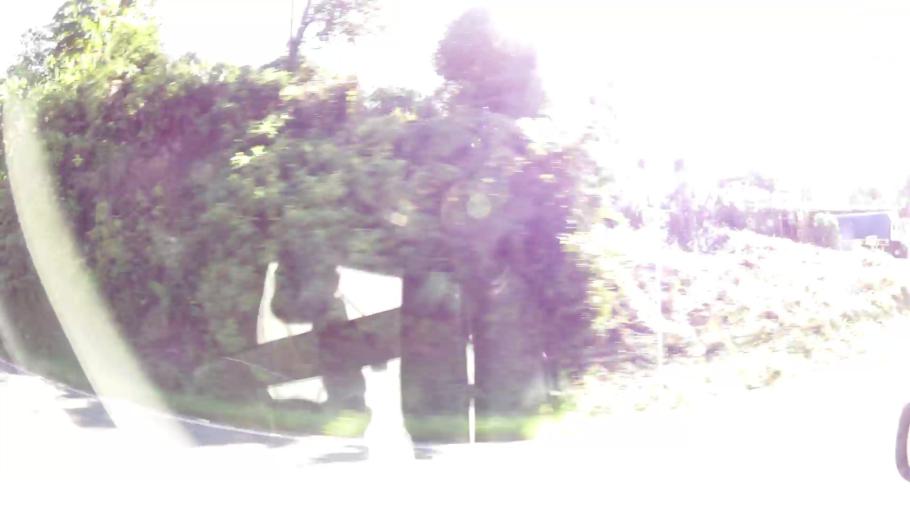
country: CR
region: San Jose
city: San Isidro
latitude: 9.3975
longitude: -83.7150
